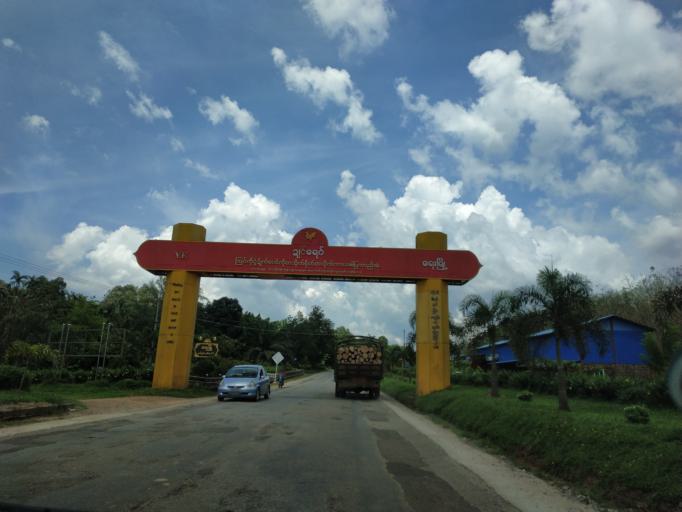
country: TH
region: Kanchanaburi
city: Sangkhla Buri
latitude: 15.2675
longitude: 97.8561
